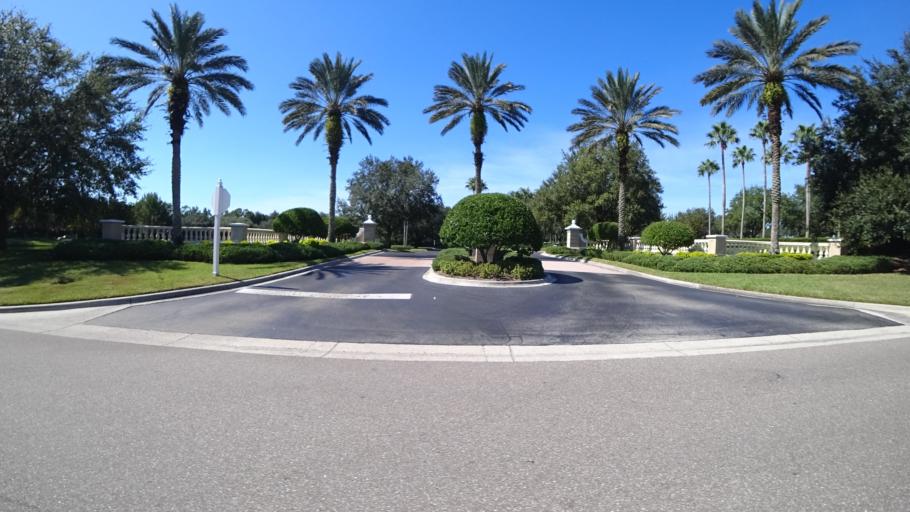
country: US
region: Florida
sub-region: Sarasota County
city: The Meadows
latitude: 27.4026
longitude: -82.4115
